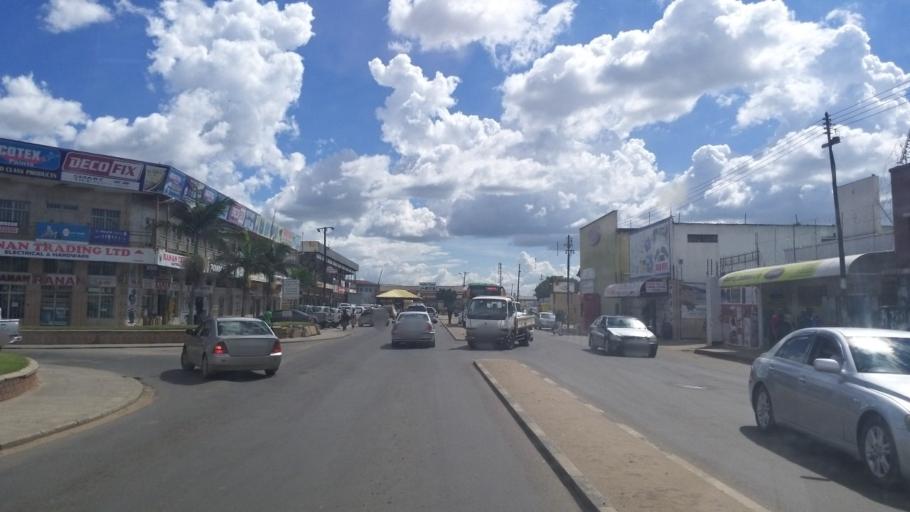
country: ZM
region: Lusaka
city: Lusaka
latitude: -15.4100
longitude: 28.2788
